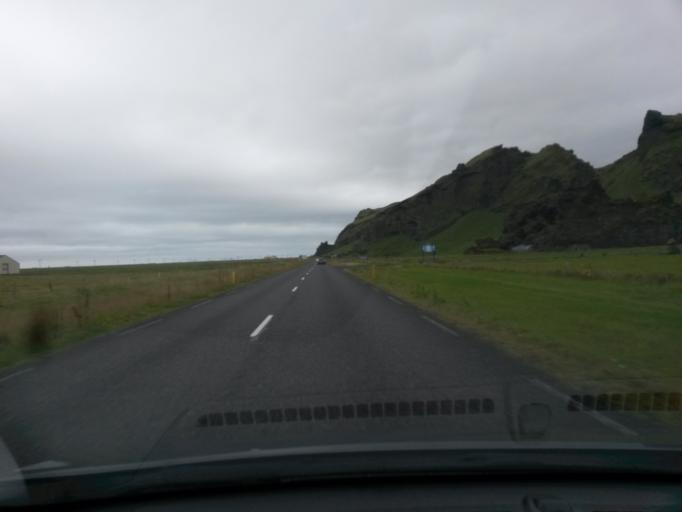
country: IS
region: South
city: Vestmannaeyjar
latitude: 63.5235
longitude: -19.5492
